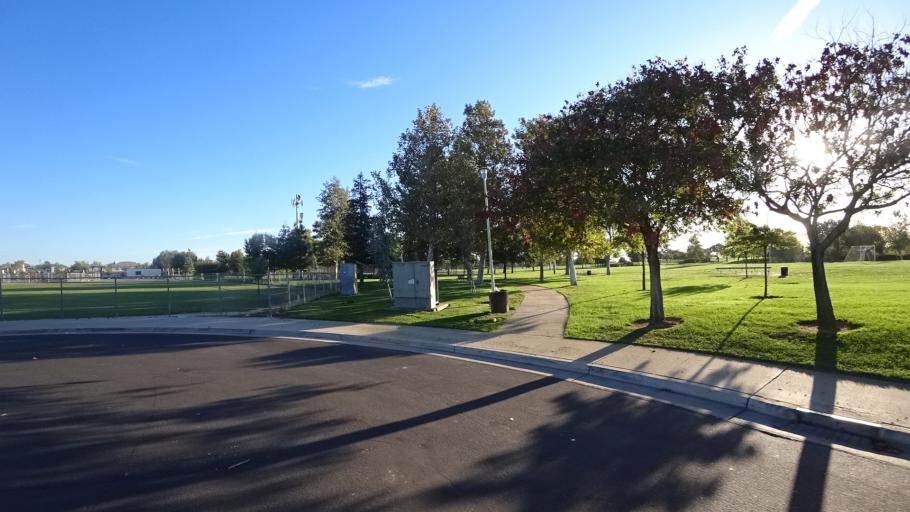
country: US
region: California
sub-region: Sacramento County
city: Laguna
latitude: 38.3953
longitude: -121.4728
